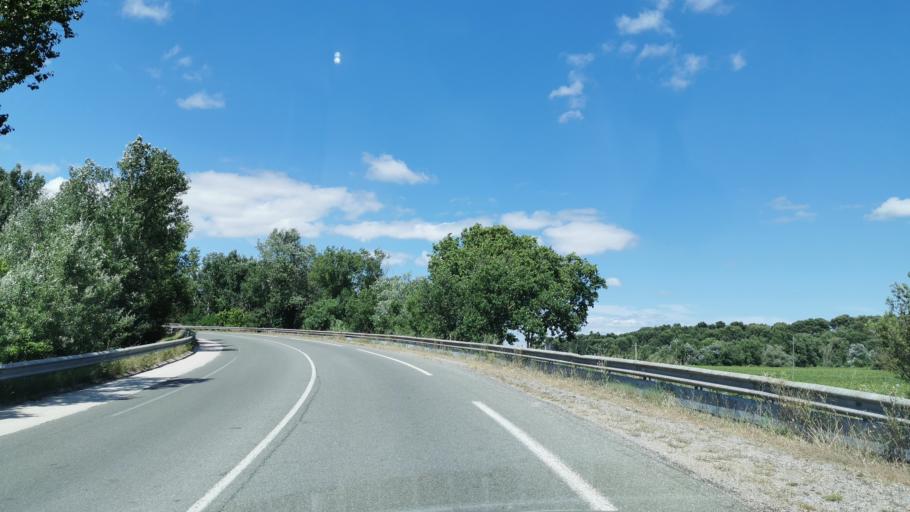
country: FR
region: Languedoc-Roussillon
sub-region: Departement de l'Aude
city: Marcorignan
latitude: 43.2325
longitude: 2.9261
